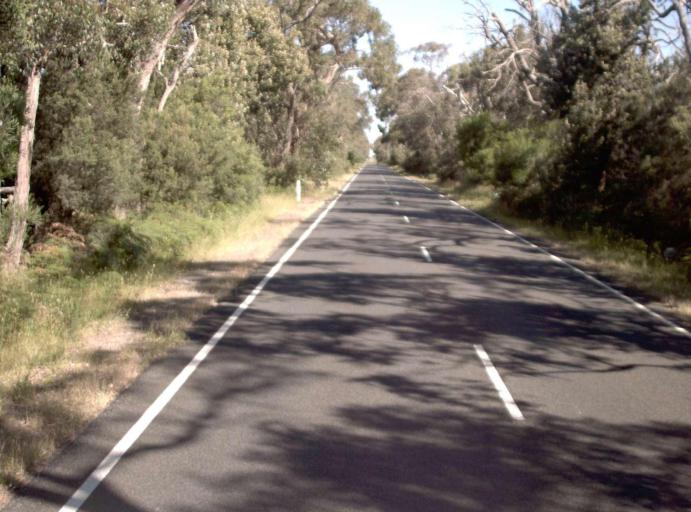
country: AU
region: Victoria
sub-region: Latrobe
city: Traralgon
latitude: -38.6588
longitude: 146.6817
